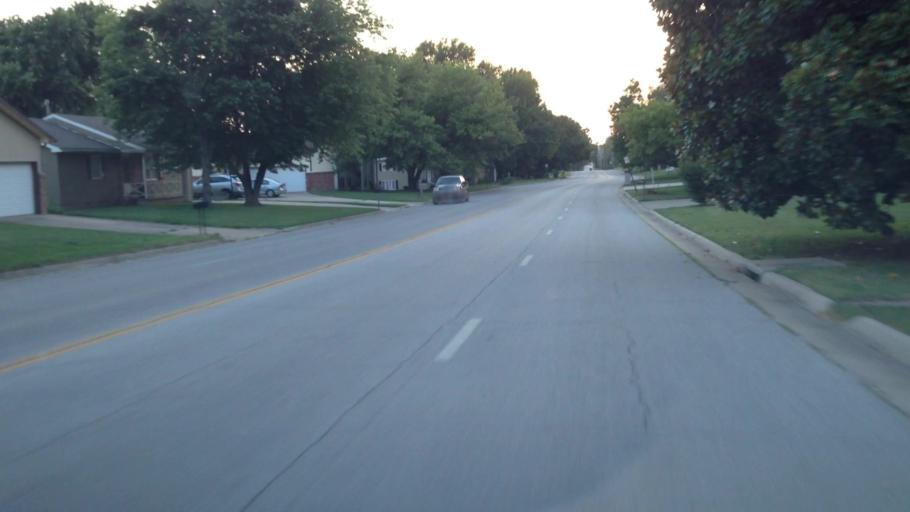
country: US
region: Kansas
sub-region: Montgomery County
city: Independence
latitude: 37.2508
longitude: -95.7072
